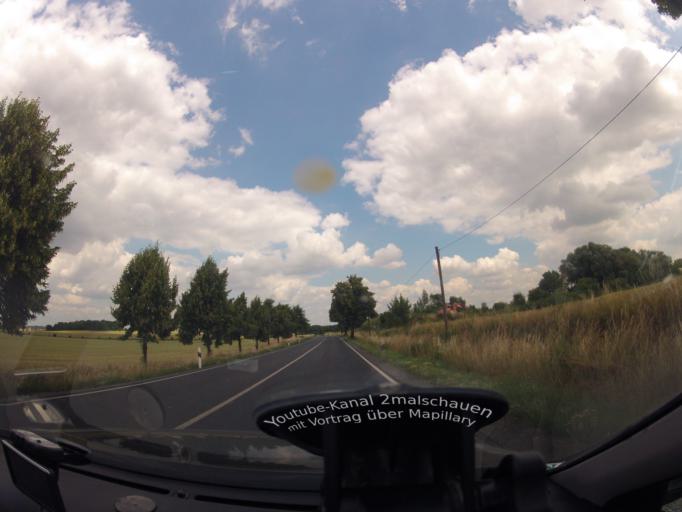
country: DE
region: Saxony
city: Jesewitz
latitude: 51.4035
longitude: 12.5315
